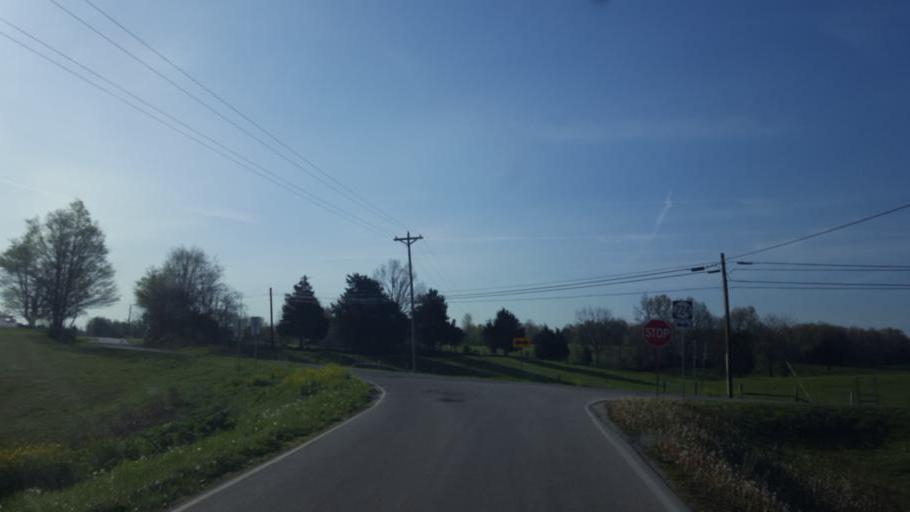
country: US
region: Kentucky
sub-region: Hart County
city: Munfordville
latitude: 37.4663
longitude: -85.9138
